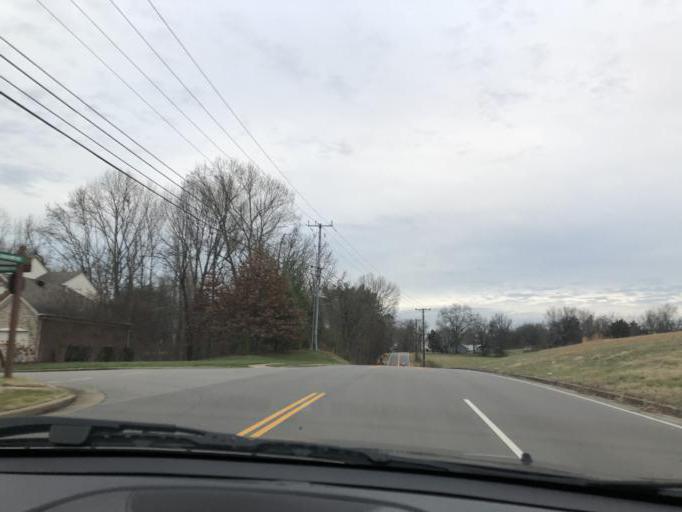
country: US
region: Tennessee
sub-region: Wilson County
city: Green Hill
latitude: 36.1887
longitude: -86.5819
